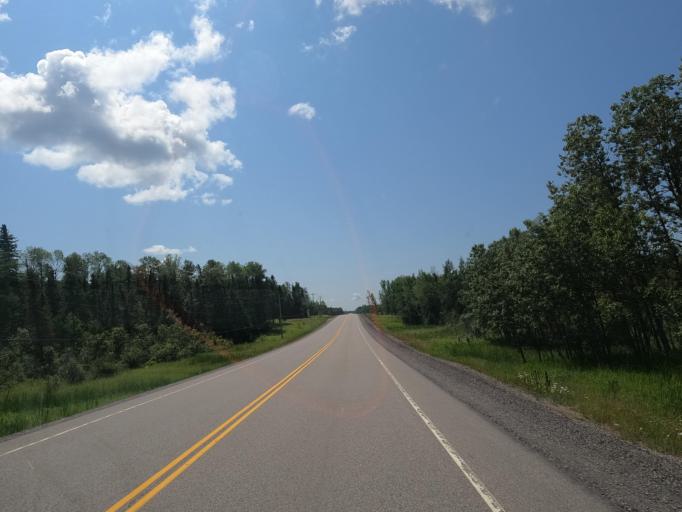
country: CA
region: Ontario
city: Dryden
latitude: 49.9188
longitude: -93.3597
